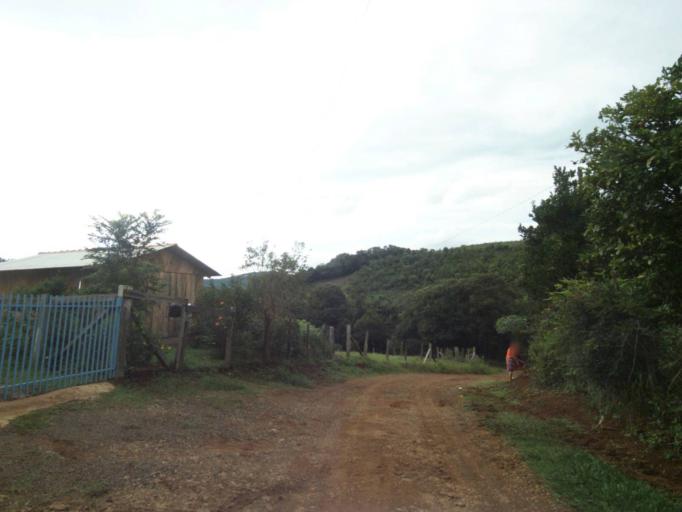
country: BR
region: Parana
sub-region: Pitanga
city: Pitanga
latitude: -24.8959
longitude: -51.9646
